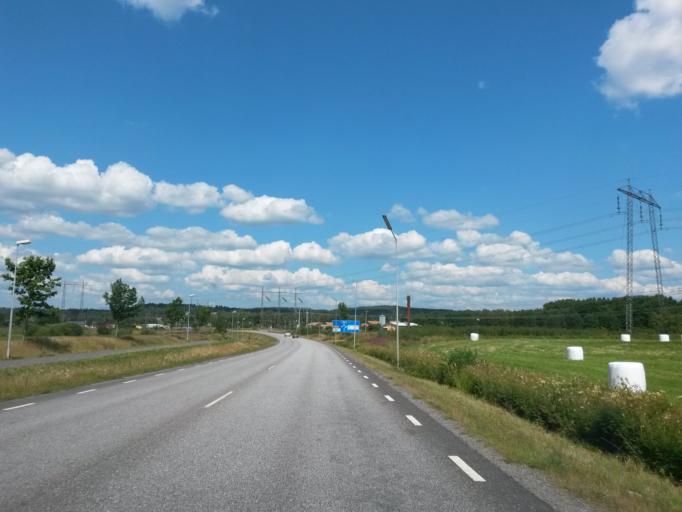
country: SE
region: Vaestra Goetaland
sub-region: Lerums Kommun
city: Grabo
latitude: 57.8318
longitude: 12.2914
